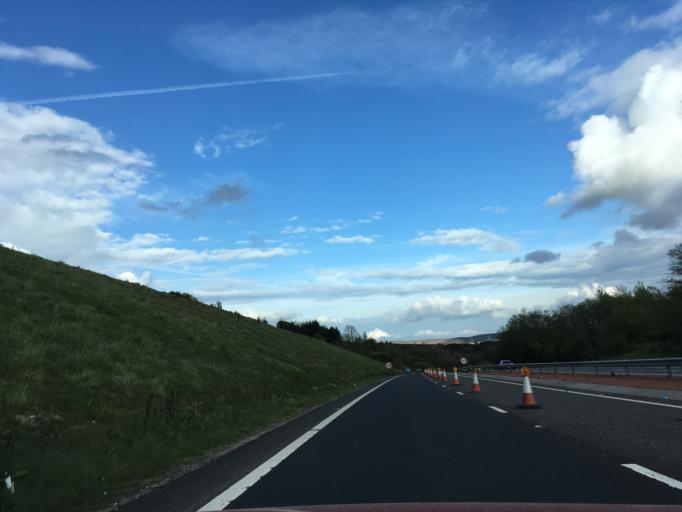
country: GB
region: Wales
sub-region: Blaenau Gwent
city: Brynmawr
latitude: 51.8094
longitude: -3.1801
